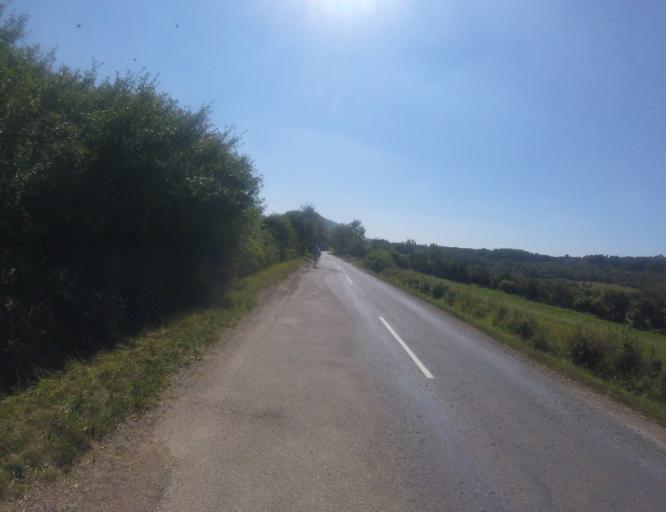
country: HU
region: Nograd
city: Bujak
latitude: 47.9486
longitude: 19.5929
